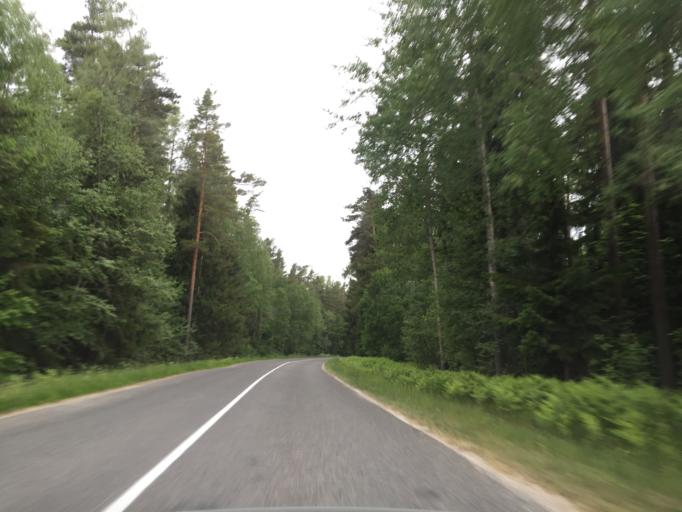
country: LV
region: Vilanu
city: Vilani
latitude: 56.5300
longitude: 26.9484
